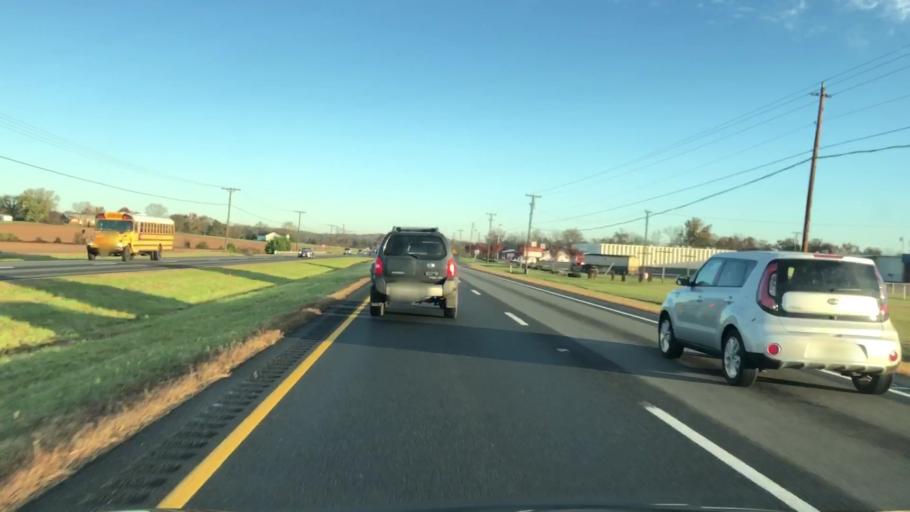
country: US
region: Virginia
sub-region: Fauquier County
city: Bealeton
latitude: 38.5352
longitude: -77.7292
